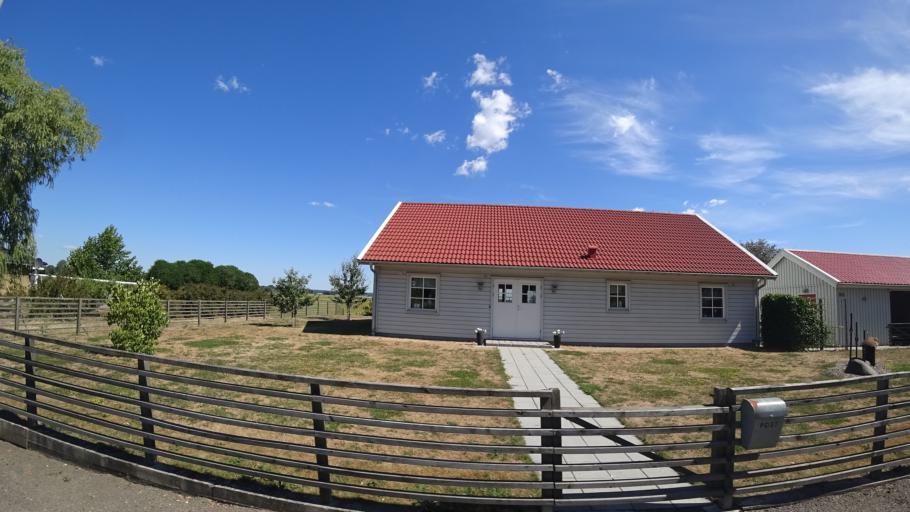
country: SE
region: Skane
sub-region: Kristianstads Kommun
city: Onnestad
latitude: 56.0457
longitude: 14.0301
